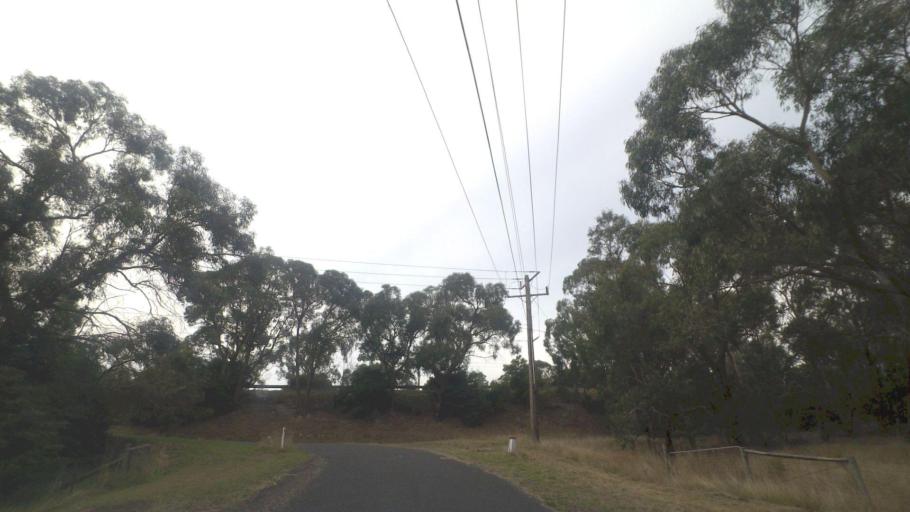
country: AU
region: Victoria
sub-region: Manningham
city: Park Orchards
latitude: -37.7673
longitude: 145.1981
